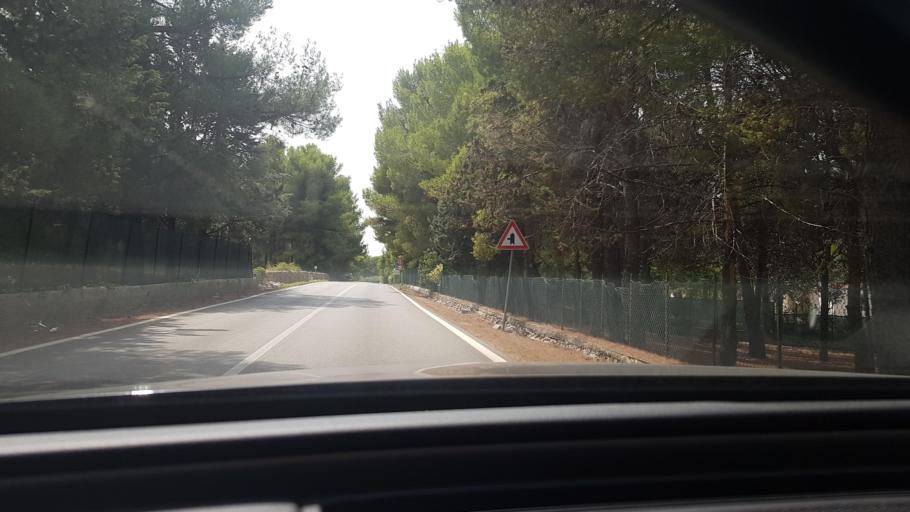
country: IT
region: Apulia
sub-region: Provincia di Barletta - Andria - Trani
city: Andria
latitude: 41.1271
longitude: 16.2880
